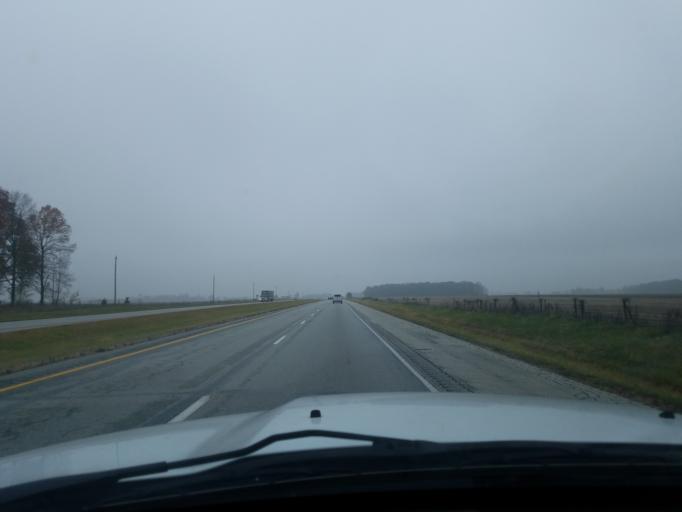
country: US
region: Indiana
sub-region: Tipton County
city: Tipton
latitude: 40.2329
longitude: -86.1278
